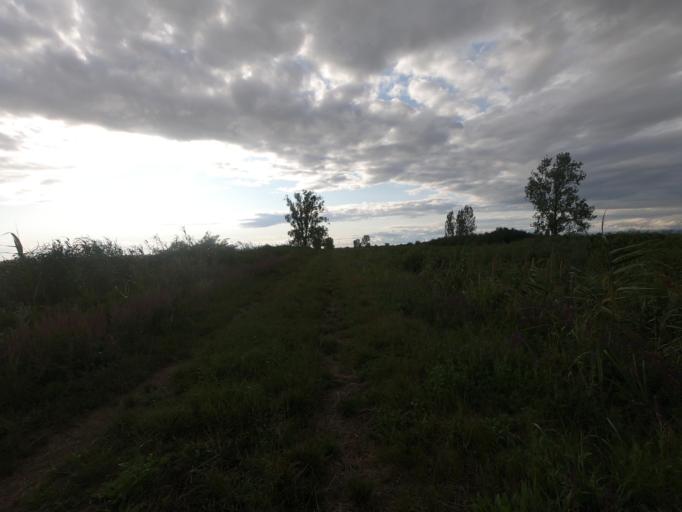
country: HU
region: Heves
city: Poroszlo
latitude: 47.7011
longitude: 20.5917
